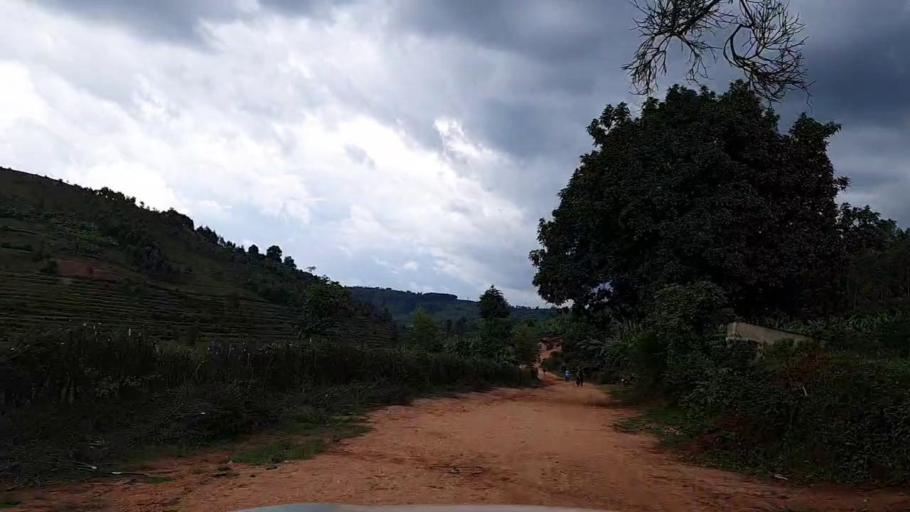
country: RW
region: Southern Province
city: Nyanza
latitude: -2.3922
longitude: 29.6864
